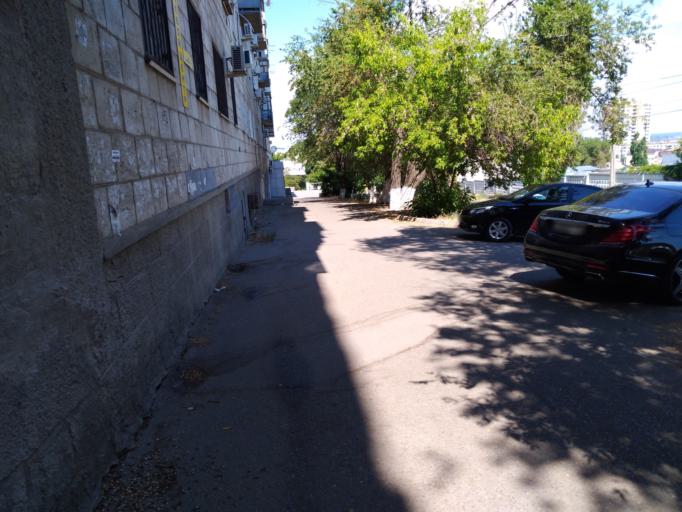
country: RU
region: Volgograd
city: Volgograd
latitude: 48.7196
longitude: 44.5219
